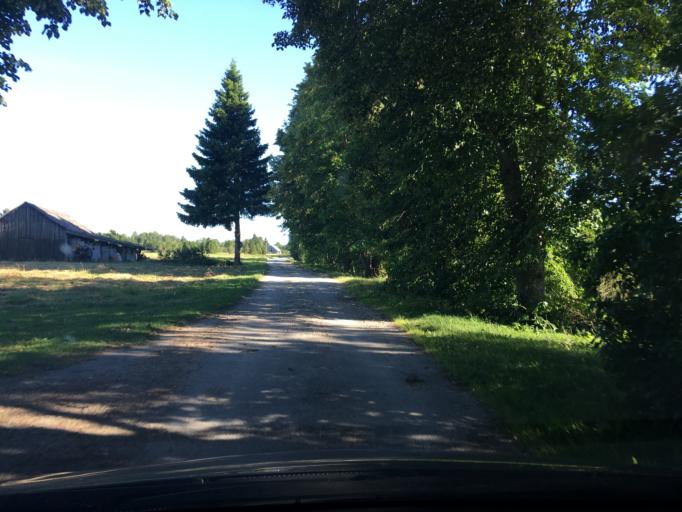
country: EE
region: Laeaene
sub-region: Lihula vald
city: Lihula
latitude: 58.5822
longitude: 23.7366
